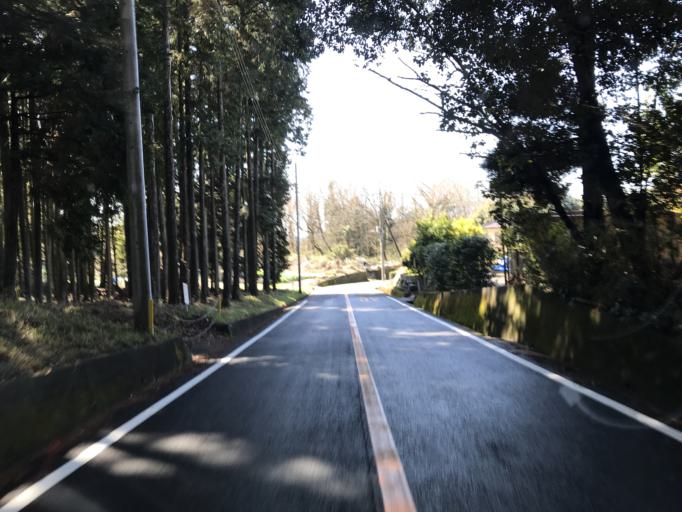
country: JP
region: Shizuoka
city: Fujinomiya
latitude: 35.2310
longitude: 138.6513
